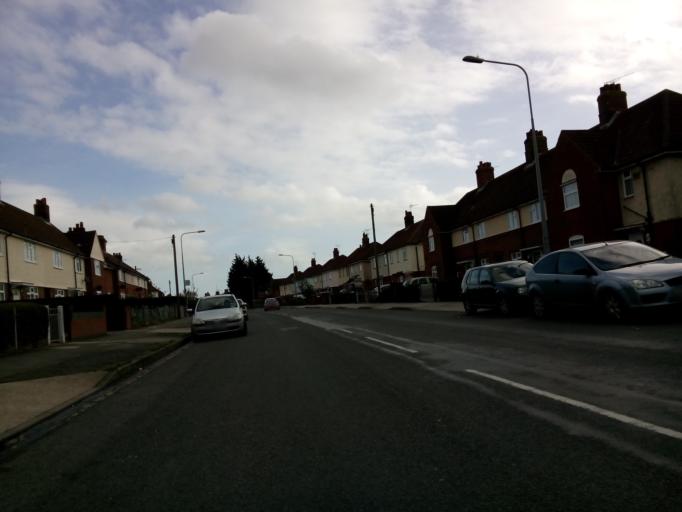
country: GB
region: England
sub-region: Suffolk
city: Ipswich
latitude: 52.0368
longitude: 1.1750
